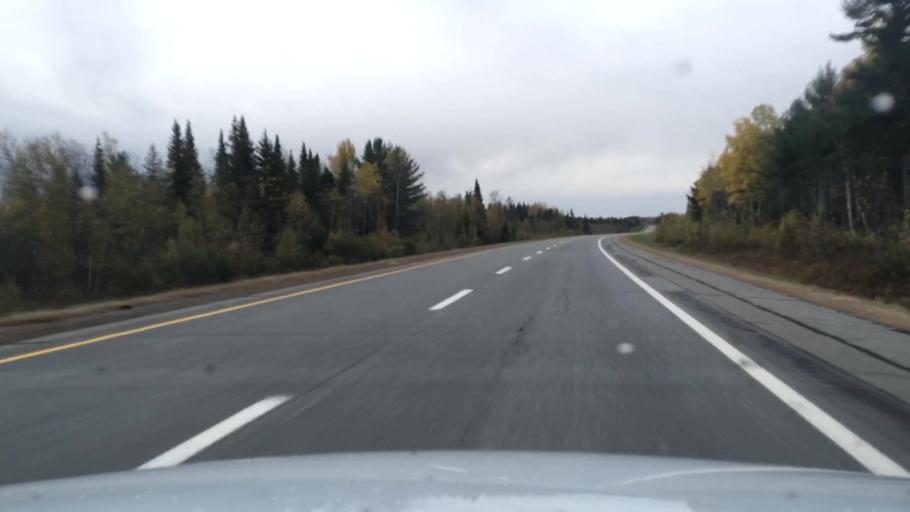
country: US
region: Maine
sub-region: Penobscot County
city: Greenbush
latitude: 45.1187
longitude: -68.6949
